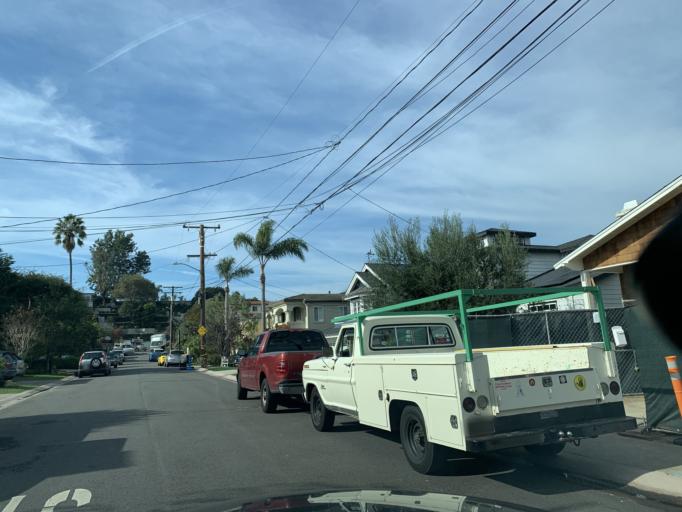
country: US
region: California
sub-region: Los Angeles County
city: Manhattan Beach
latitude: 33.8810
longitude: -118.3939
